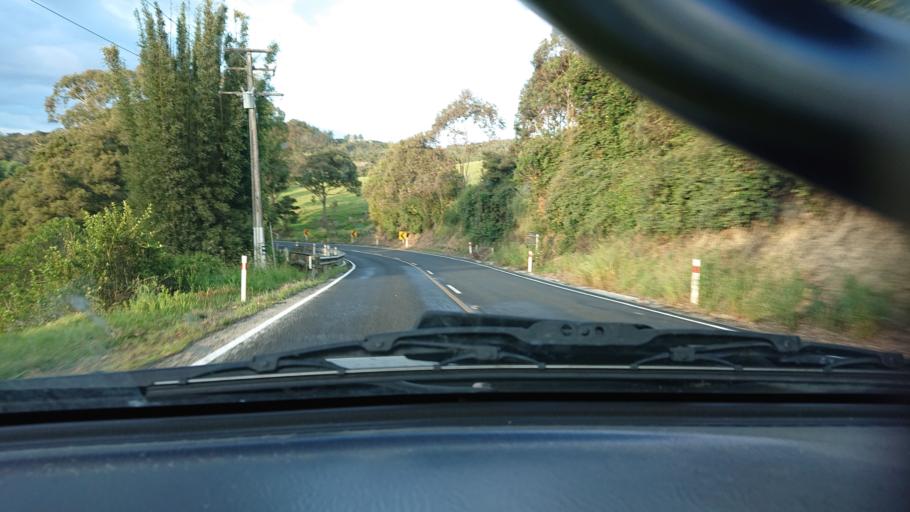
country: NZ
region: Auckland
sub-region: Auckland
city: Parakai
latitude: -36.5363
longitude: 174.4567
